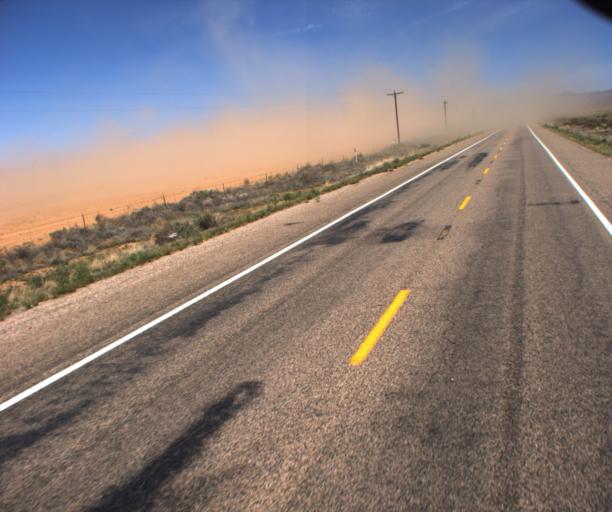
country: US
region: Arizona
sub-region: Mohave County
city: New Kingman-Butler
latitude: 35.3467
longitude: -113.8868
